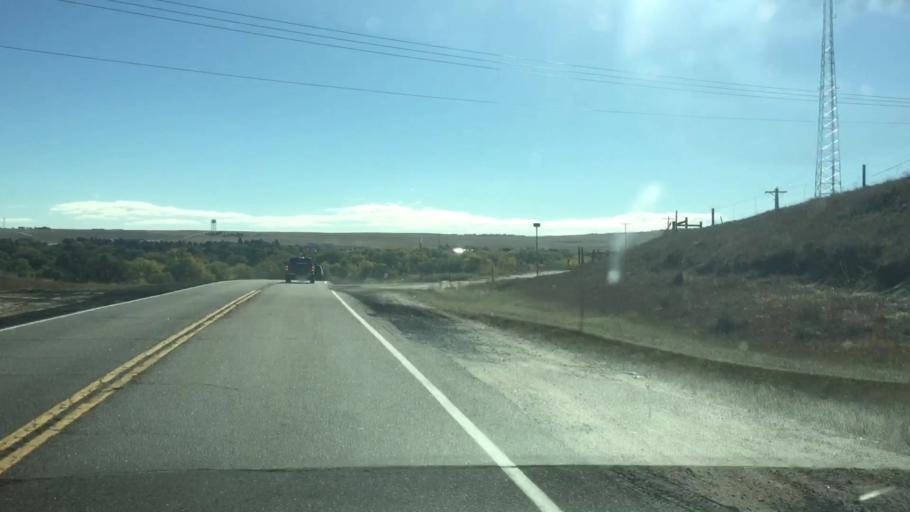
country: US
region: Colorado
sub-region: Elbert County
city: Kiowa
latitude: 39.3484
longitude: -104.4788
